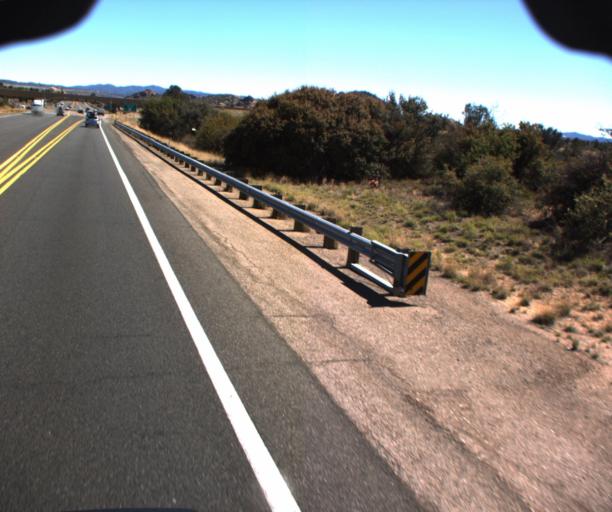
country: US
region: Arizona
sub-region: Yavapai County
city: Prescott
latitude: 34.6355
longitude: -112.4300
